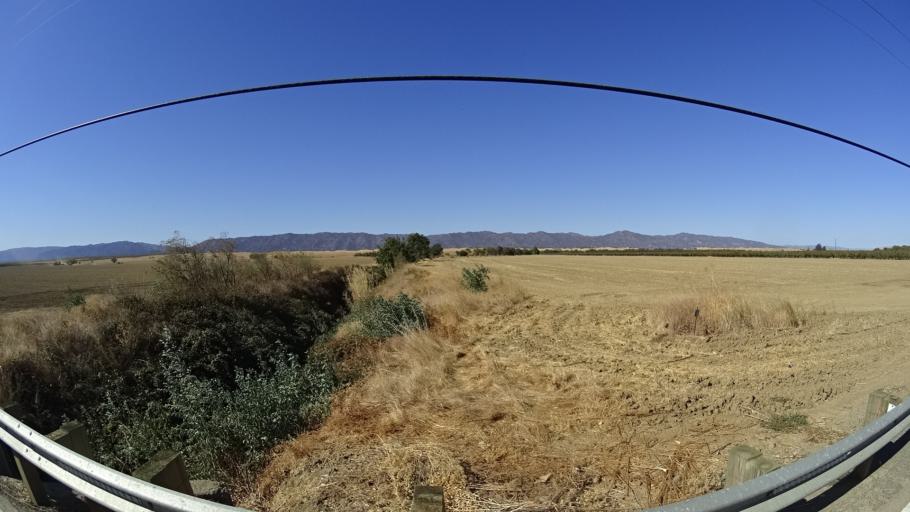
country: US
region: California
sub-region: Yolo County
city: Winters
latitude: 38.5753
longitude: -121.9714
